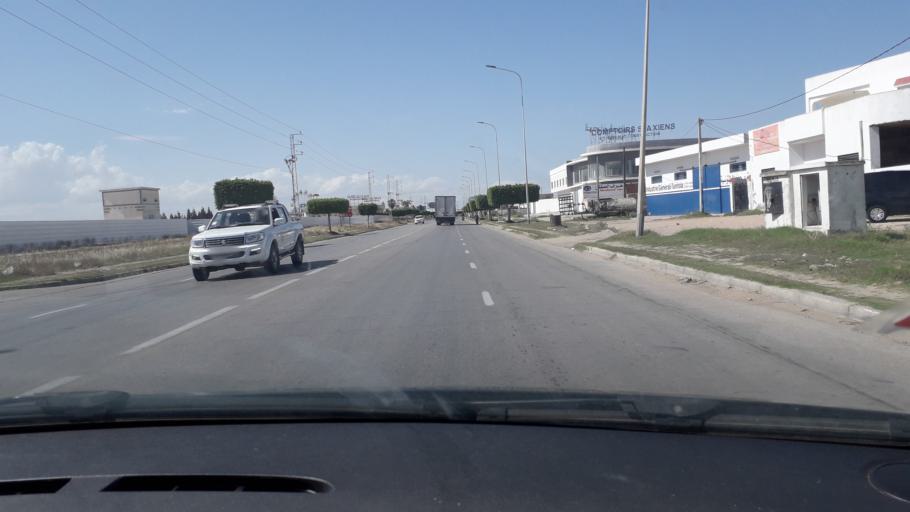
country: TN
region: Safaqis
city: Al Qarmadah
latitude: 34.8402
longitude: 10.7641
